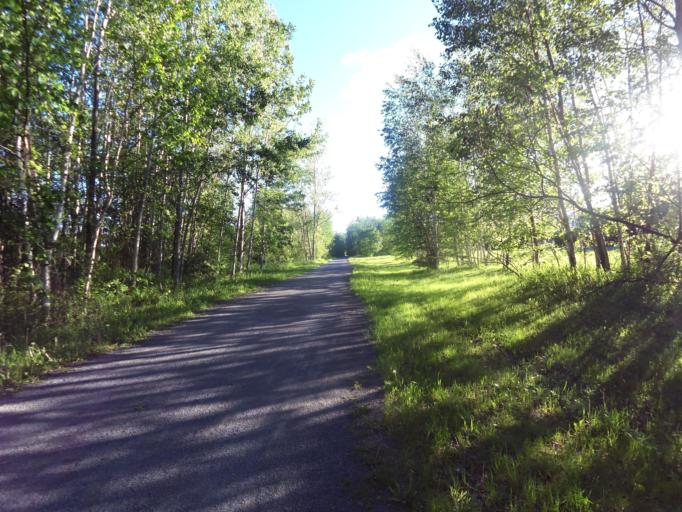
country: CA
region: Ontario
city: Bells Corners
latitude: 45.2672
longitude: -75.9064
